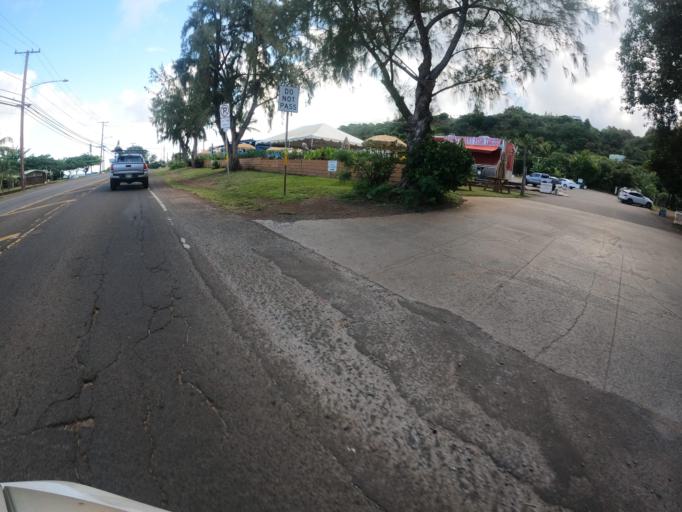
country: US
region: Hawaii
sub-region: Honolulu County
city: Pupukea
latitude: 21.6492
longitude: -158.0621
